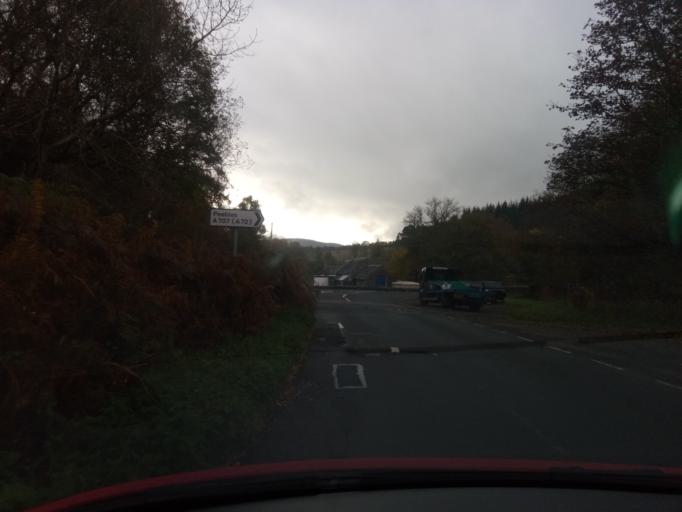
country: GB
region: Scotland
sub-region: The Scottish Borders
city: Selkirk
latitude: 55.6060
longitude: -2.8767
